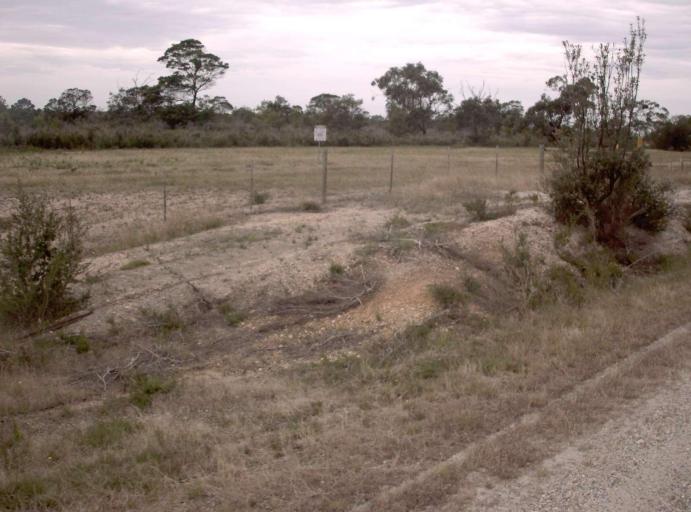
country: AU
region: Victoria
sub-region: Wellington
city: Sale
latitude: -38.1901
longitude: 147.2797
